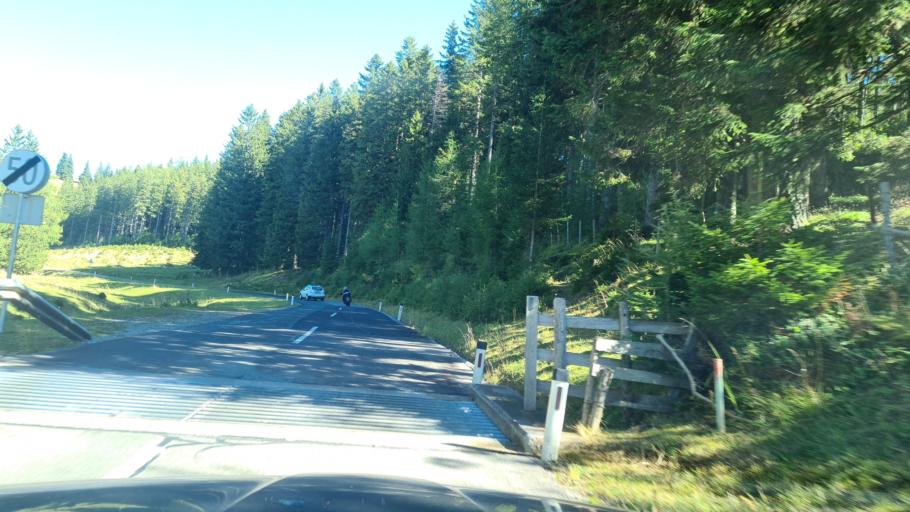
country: AT
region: Styria
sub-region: Politischer Bezirk Weiz
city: Gasen
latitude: 47.3449
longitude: 15.5434
